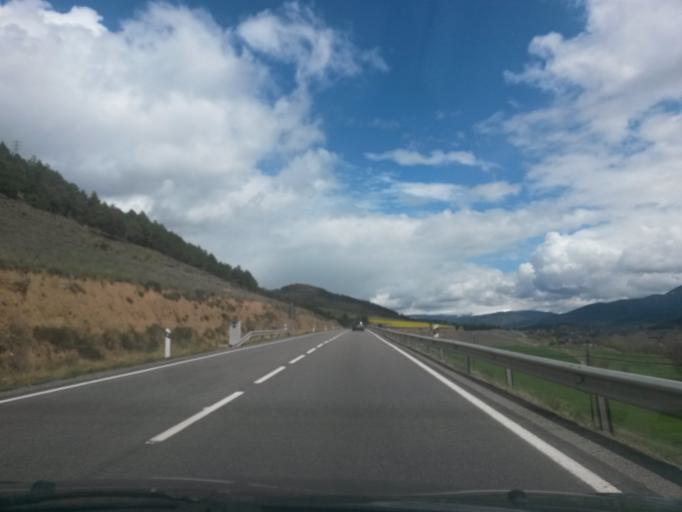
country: ES
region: Catalonia
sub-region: Provincia de Lleida
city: Bellver de Cerdanya
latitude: 42.3731
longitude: 1.7472
